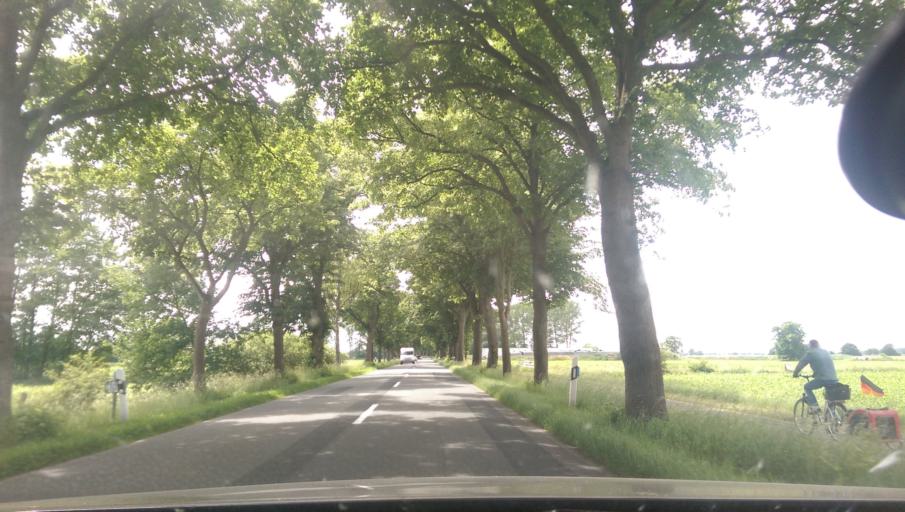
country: DE
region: Lower Saxony
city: Oyten
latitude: 53.0905
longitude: 9.0514
